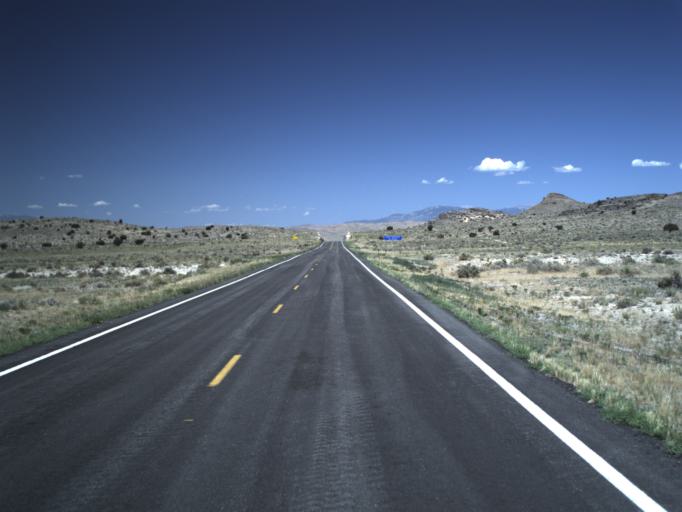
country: US
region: Utah
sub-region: Beaver County
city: Milford
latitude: 39.0776
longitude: -113.6903
